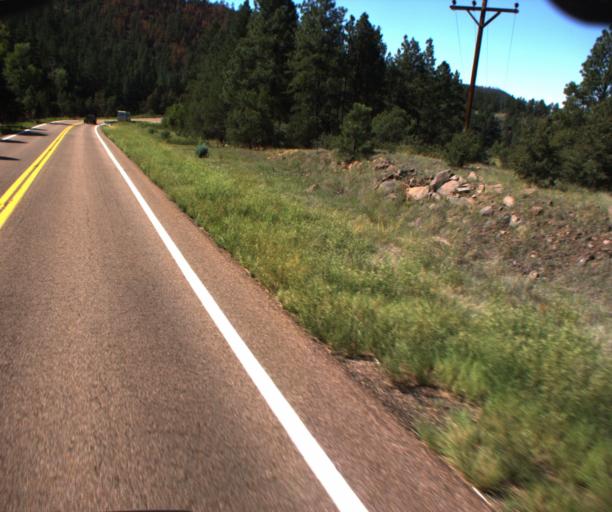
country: US
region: Arizona
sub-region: Navajo County
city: Linden
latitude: 34.0731
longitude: -110.1934
